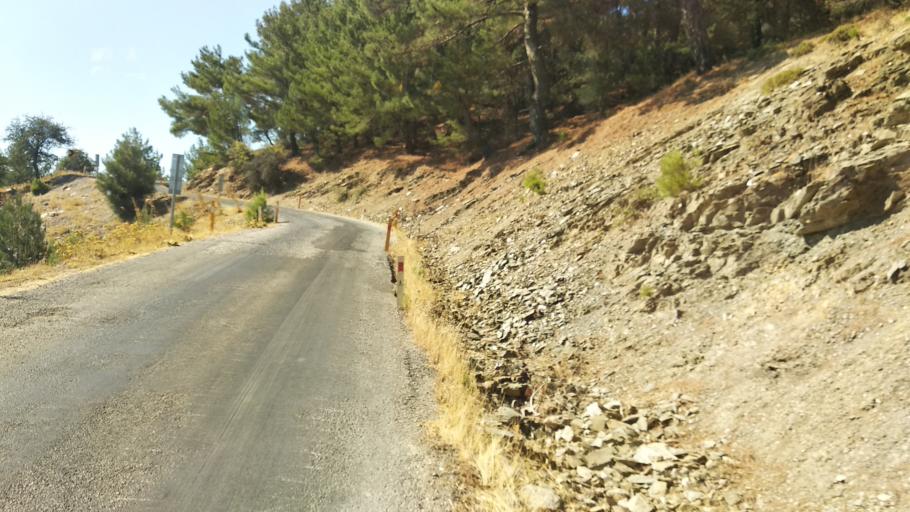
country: TR
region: Izmir
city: Gaziemir
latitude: 38.2966
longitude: 26.9994
